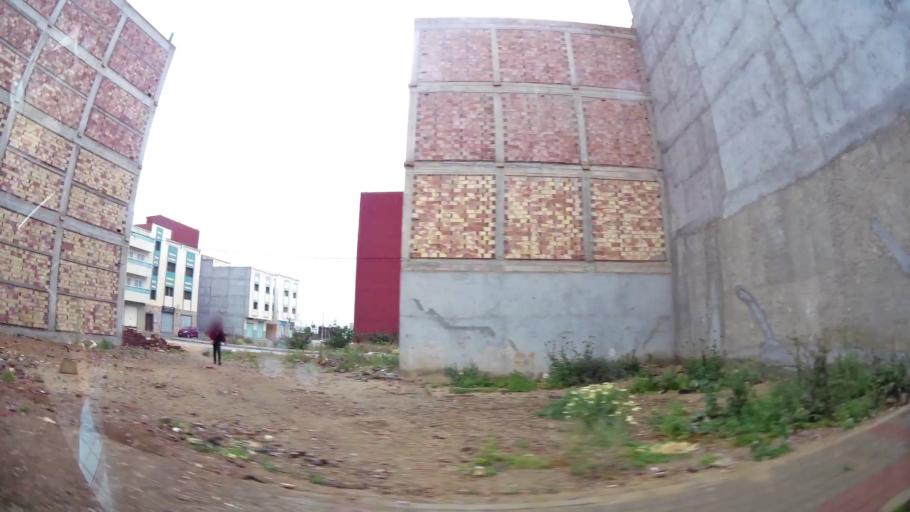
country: MA
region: Taza-Al Hoceima-Taounate
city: Imzourene
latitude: 35.1417
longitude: -3.8494
